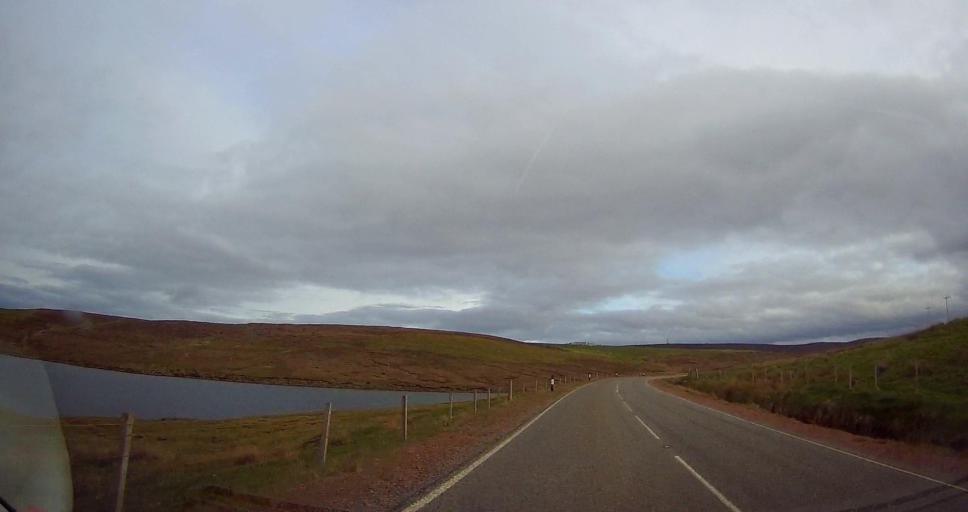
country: GB
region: Scotland
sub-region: Shetland Islands
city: Lerwick
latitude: 60.4626
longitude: -1.2104
